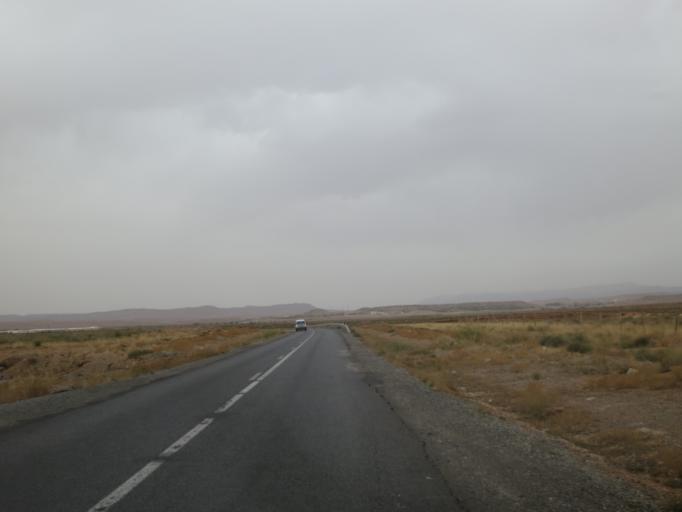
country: MA
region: Meknes-Tafilalet
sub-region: Khenifra
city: Midelt
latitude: 32.6975
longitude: -4.8249
